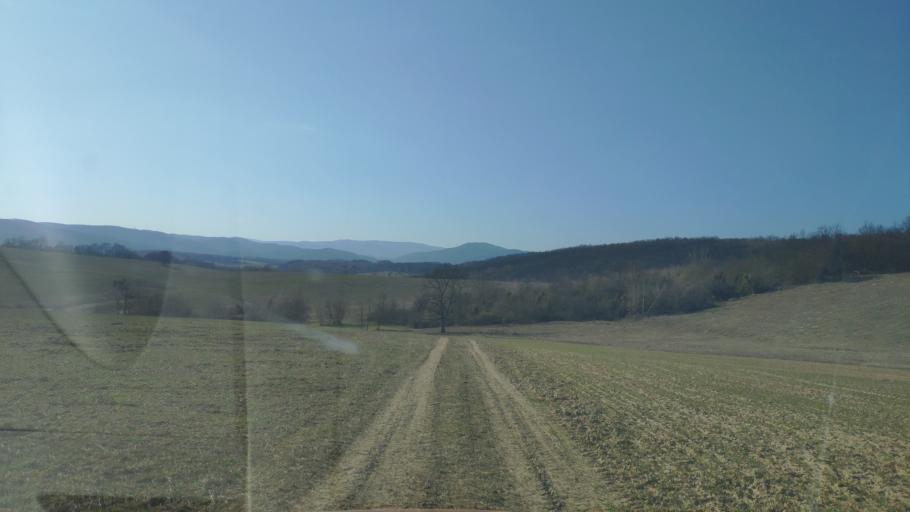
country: SK
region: Banskobystricky
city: Revuca
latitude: 48.5517
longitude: 20.2658
